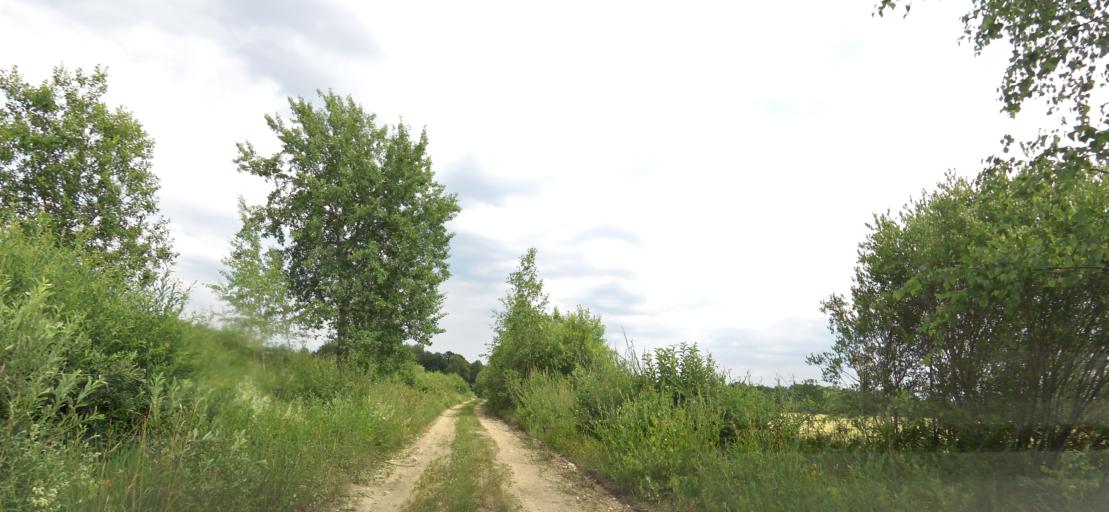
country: LT
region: Panevezys
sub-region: Birzai
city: Birzai
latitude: 56.3598
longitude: 24.9630
